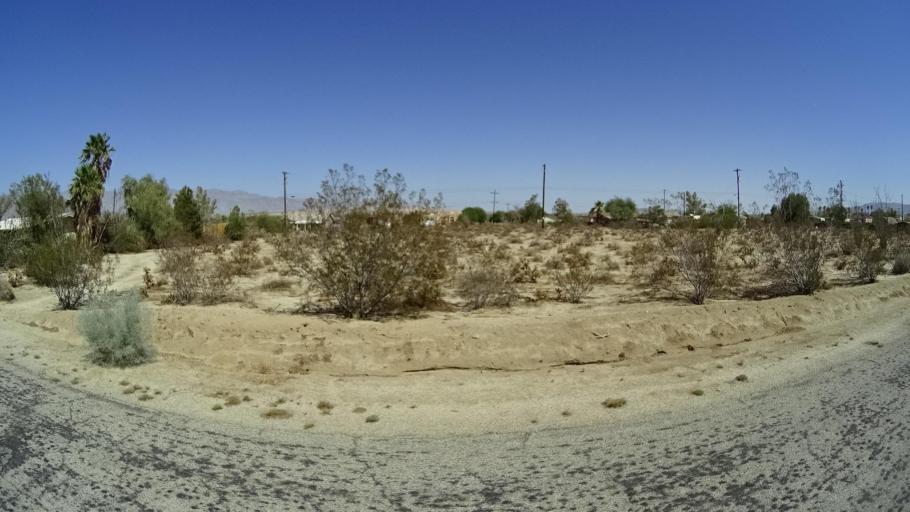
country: US
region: California
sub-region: San Diego County
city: Borrego Springs
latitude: 33.2260
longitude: -116.3687
